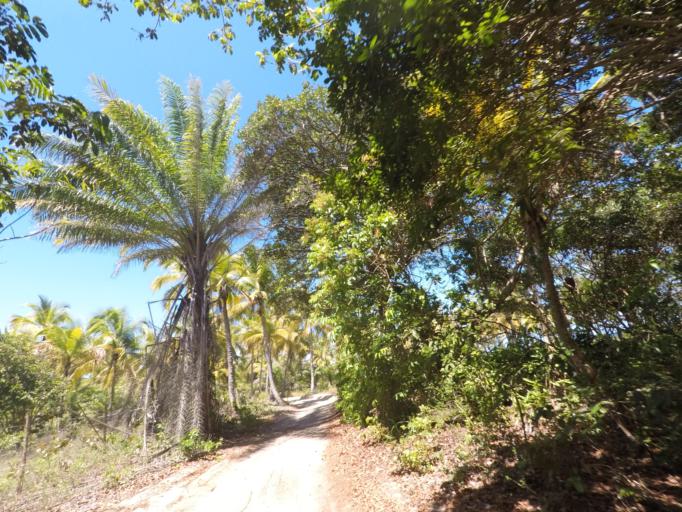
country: BR
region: Bahia
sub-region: Marau
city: Marau
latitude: -14.0073
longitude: -38.9451
